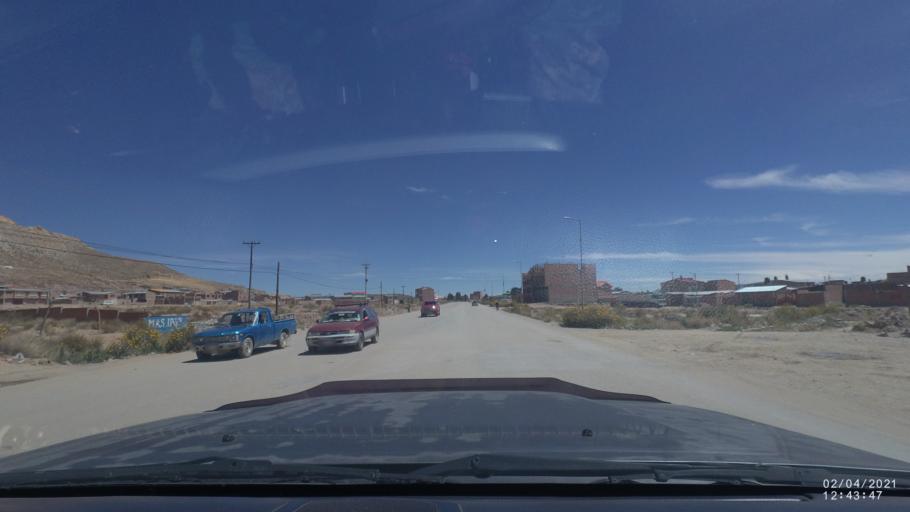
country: BO
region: Oruro
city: Oruro
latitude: -17.9274
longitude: -67.1232
